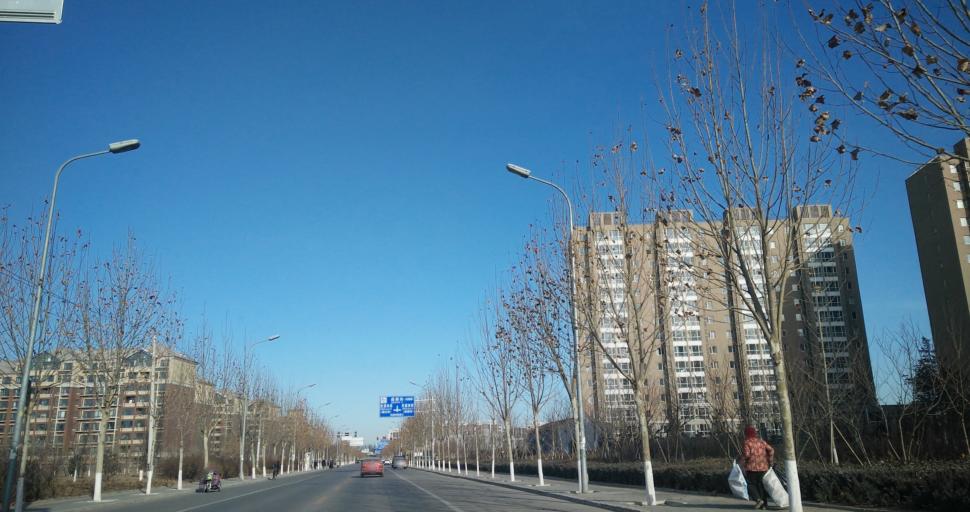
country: CN
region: Beijing
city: Yinghai
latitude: 39.7090
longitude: 116.3979
